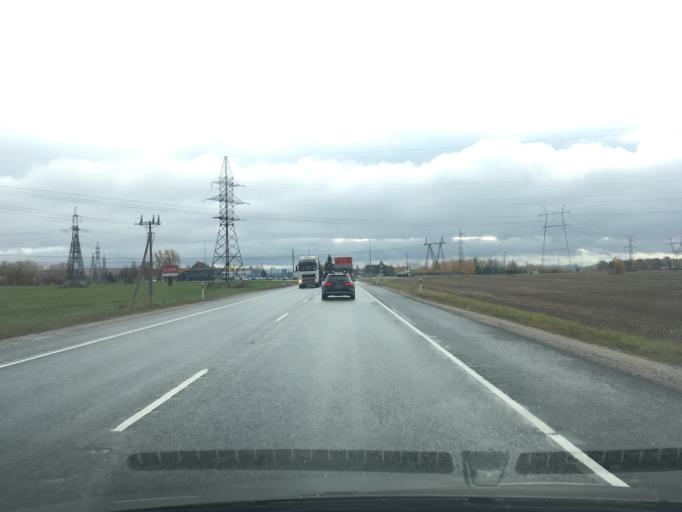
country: EE
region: Tartu
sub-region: Tartu linn
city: Tartu
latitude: 58.3821
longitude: 26.6731
